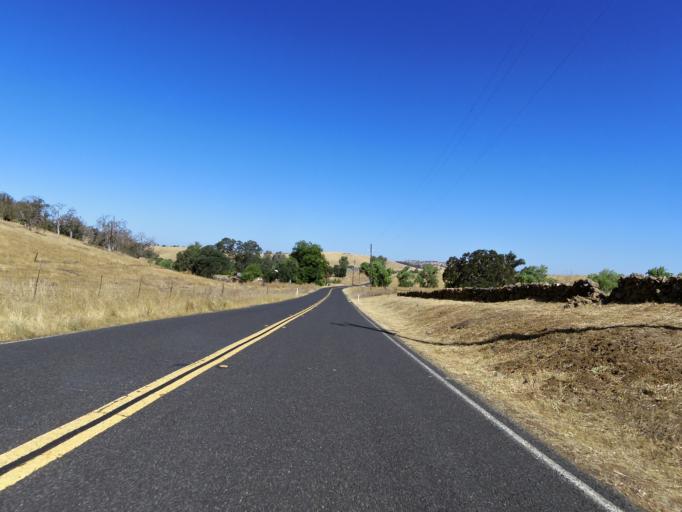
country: US
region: California
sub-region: Merced County
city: Planada
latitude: 37.4965
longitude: -120.2307
